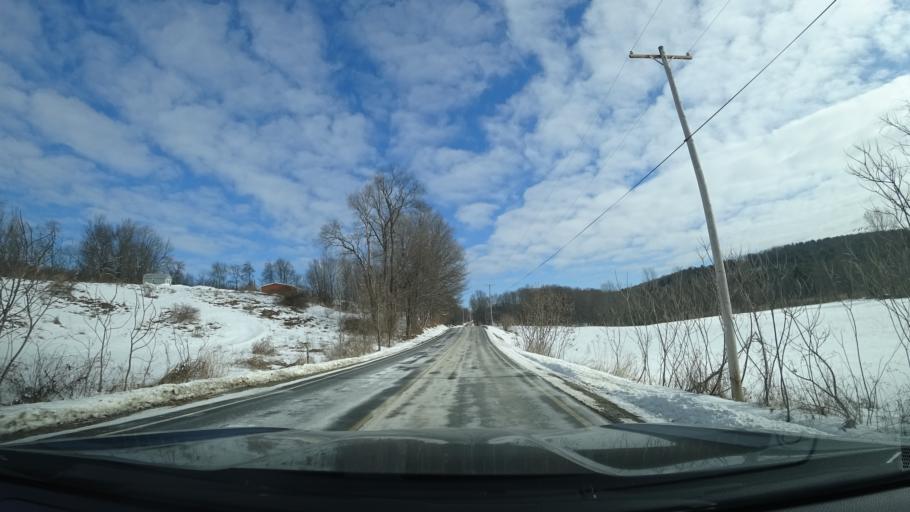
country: US
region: New York
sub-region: Washington County
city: Fort Edward
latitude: 43.2445
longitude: -73.4334
